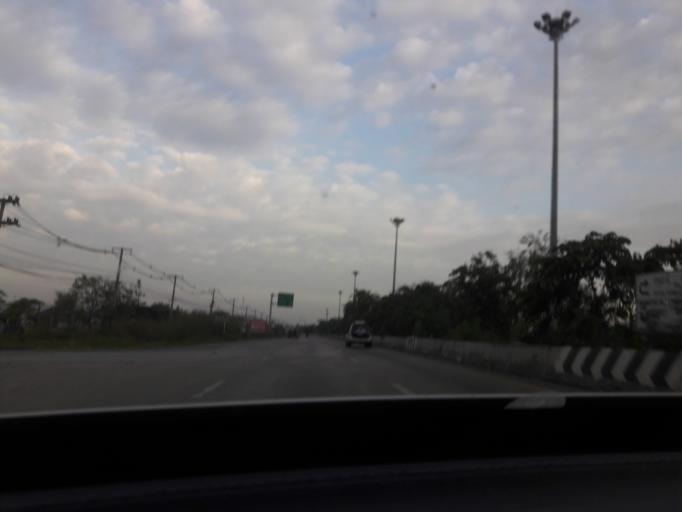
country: TH
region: Phra Nakhon Si Ayutthaya
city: Bang Pa-in
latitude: 14.1649
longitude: 100.5643
